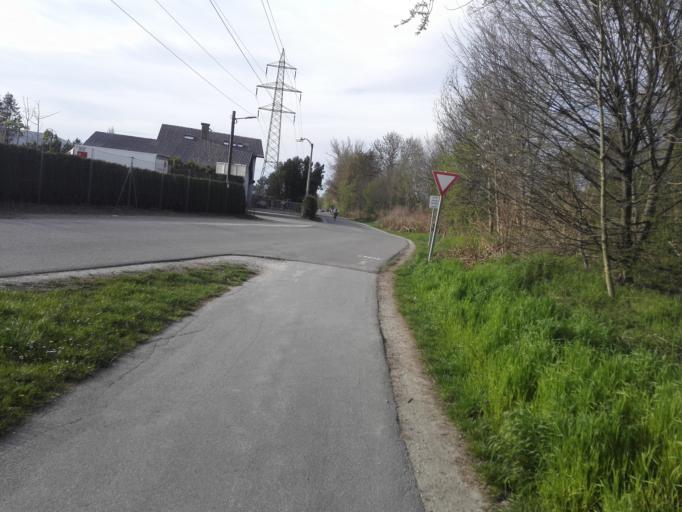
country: AT
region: Styria
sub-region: Politischer Bezirk Graz-Umgebung
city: Feldkirchen bei Graz
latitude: 47.0266
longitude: 15.4526
